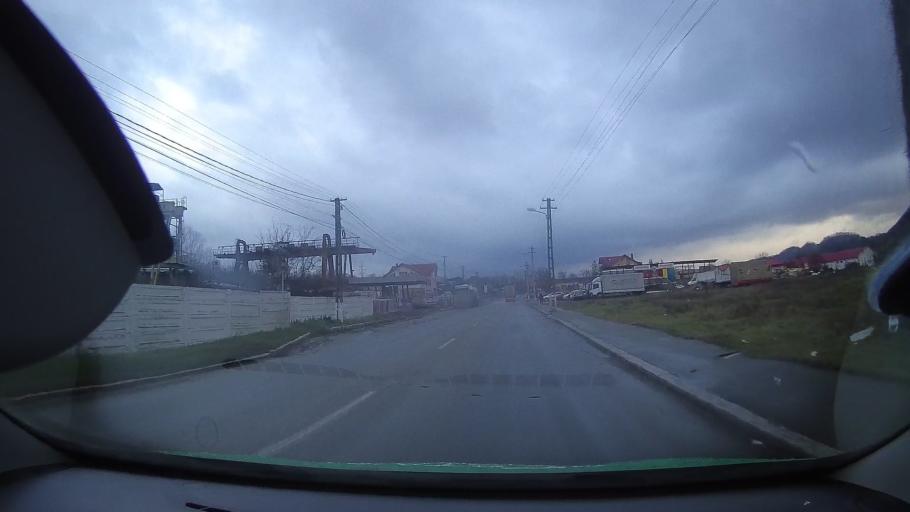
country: RO
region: Hunedoara
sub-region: Municipiul Brad
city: Brad
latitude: 46.1378
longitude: 22.7789
